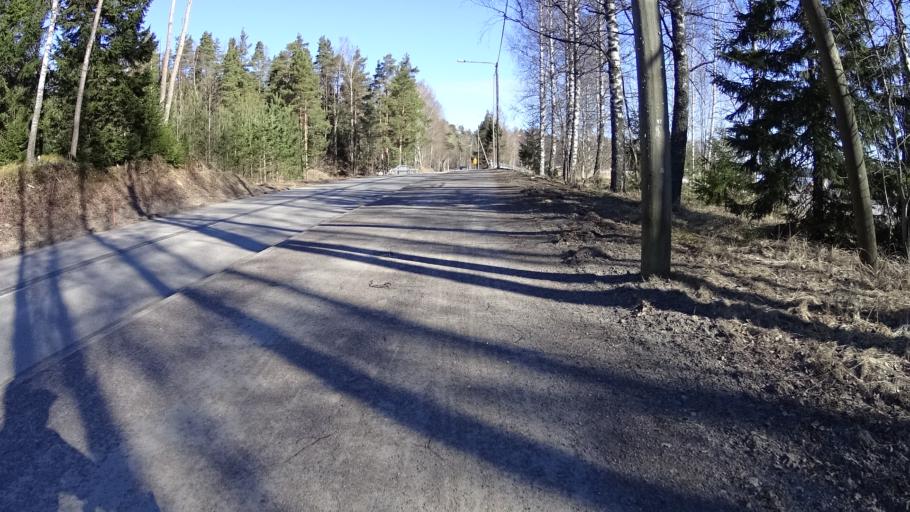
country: FI
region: Uusimaa
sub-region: Helsinki
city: Espoo
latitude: 60.2391
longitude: 24.6558
